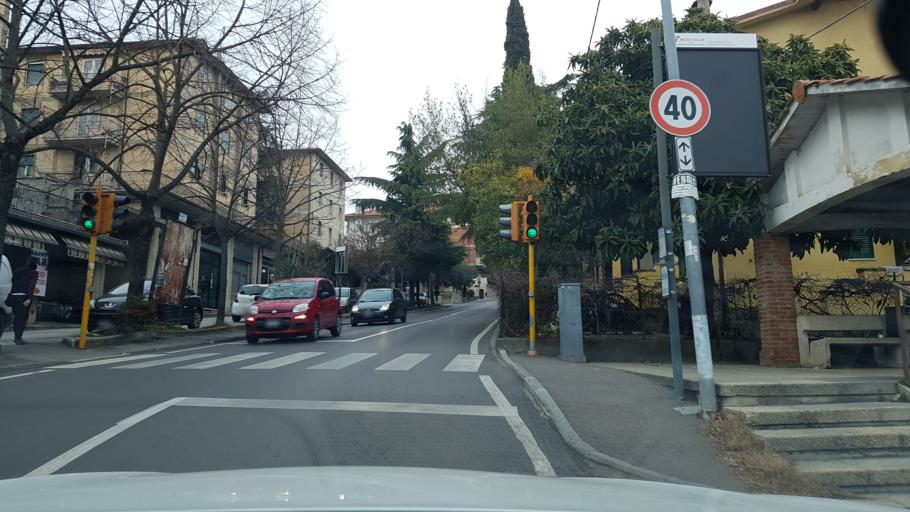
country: IT
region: Umbria
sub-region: Provincia di Perugia
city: Perugia
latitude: 43.1178
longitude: 12.3646
